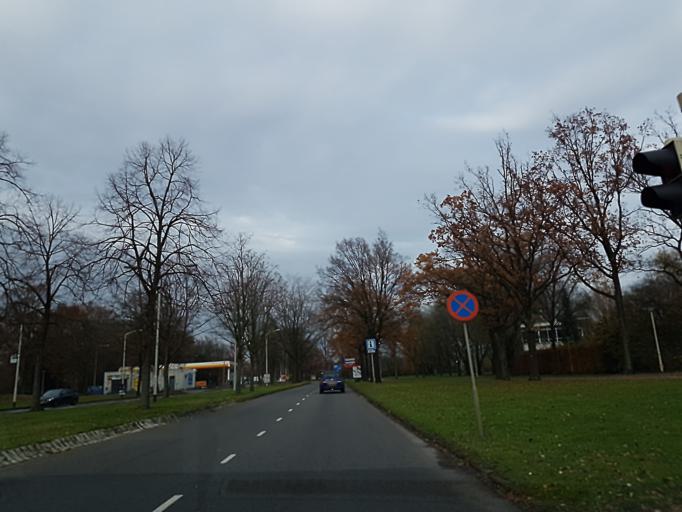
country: NL
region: North Brabant
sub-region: Roosendaal
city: Roosendaal
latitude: 51.5260
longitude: 4.4656
